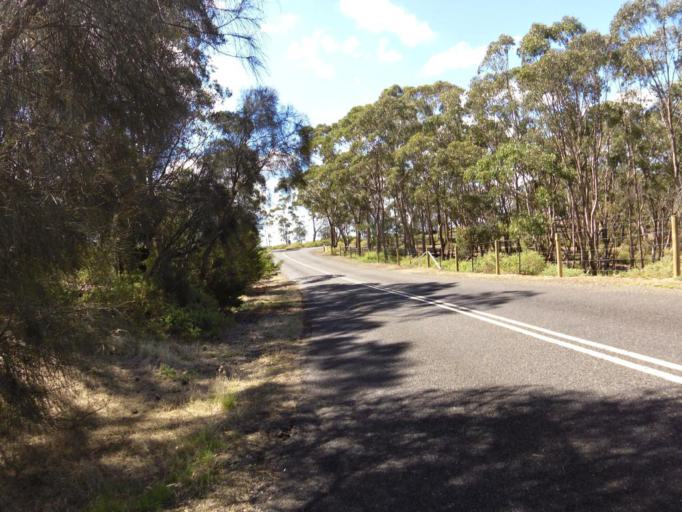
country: AU
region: Victoria
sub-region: Brimbank
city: Sydenham
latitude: -37.6686
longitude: 144.7656
